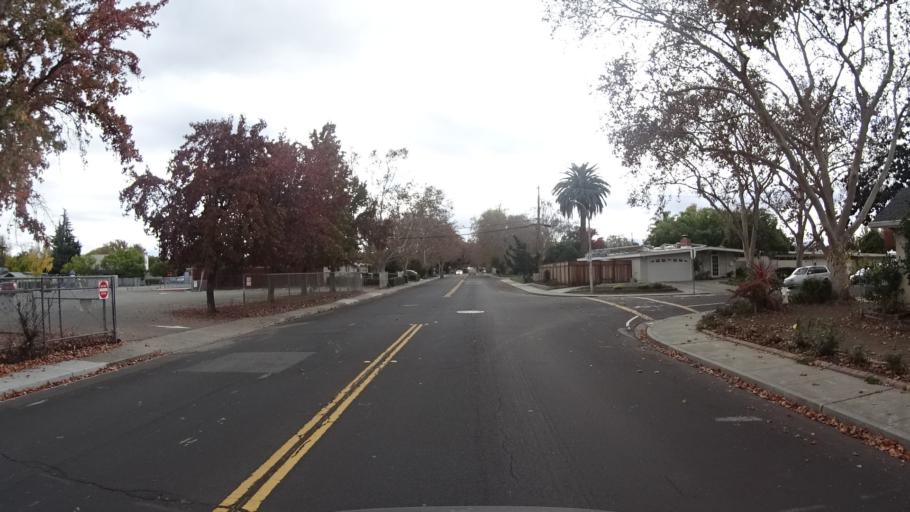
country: US
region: California
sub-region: Santa Clara County
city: Santa Clara
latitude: 37.3287
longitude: -121.9811
